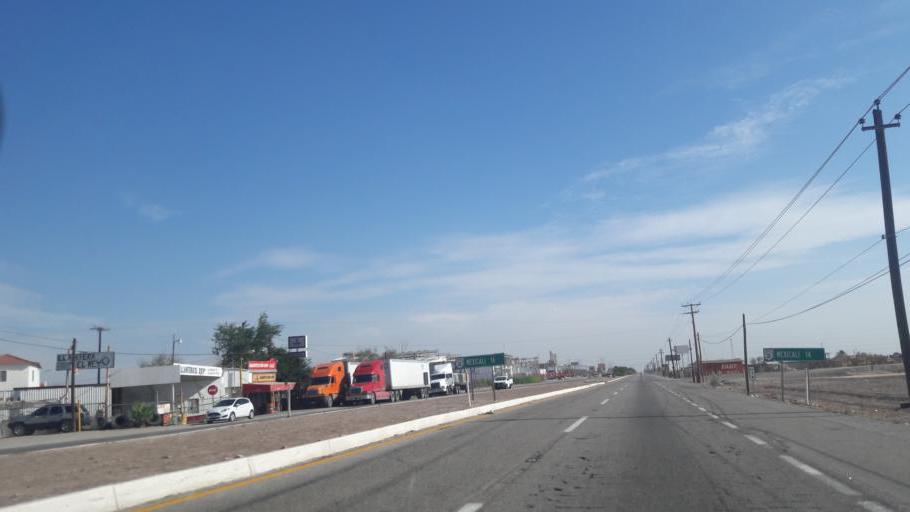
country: MX
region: Baja California
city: Progreso
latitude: 32.6004
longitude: -115.6511
